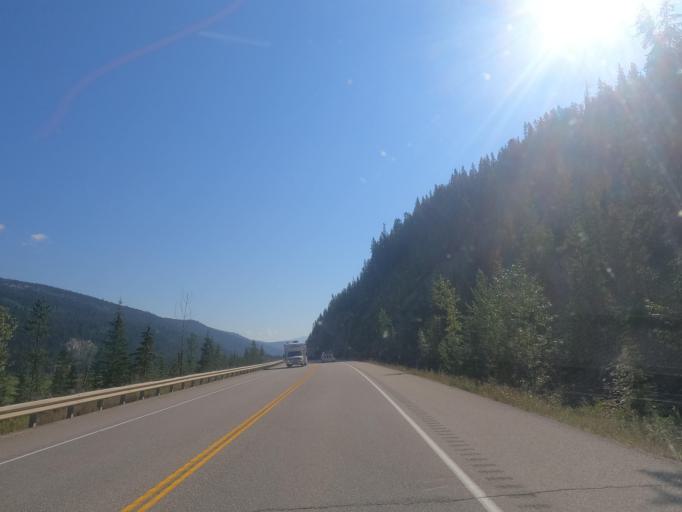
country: CA
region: Alberta
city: Jasper Park Lodge
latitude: 52.8769
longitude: -118.3391
